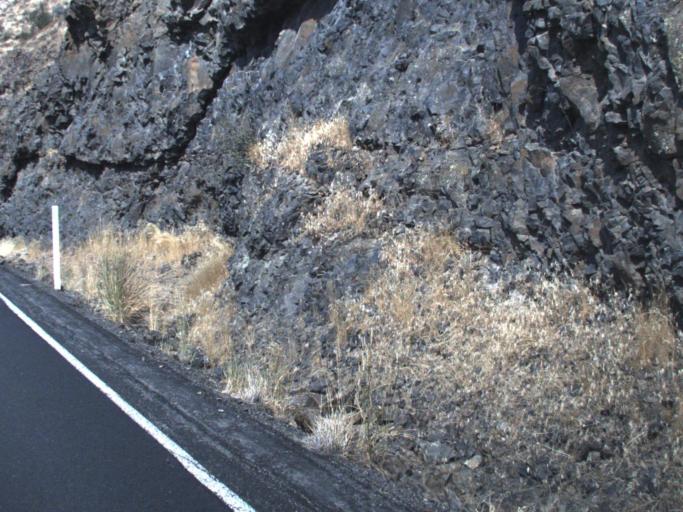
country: US
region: Washington
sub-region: Kittitas County
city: Kittitas
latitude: 46.8646
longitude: -120.4786
